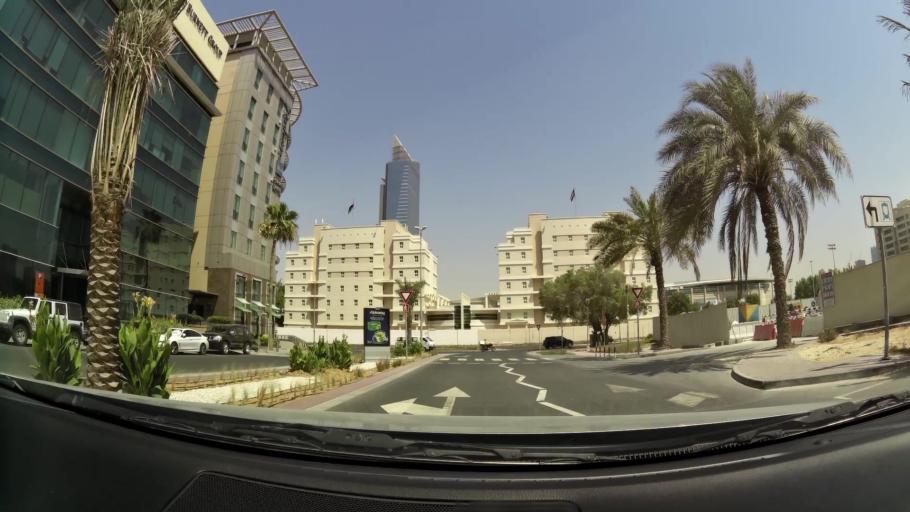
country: AE
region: Dubai
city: Dubai
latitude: 25.0937
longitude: 55.1547
